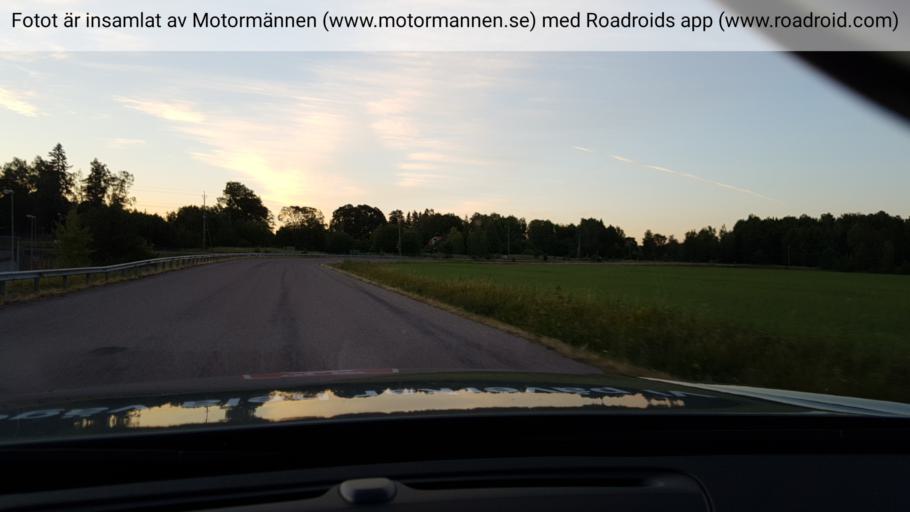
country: SE
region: Vaestmanland
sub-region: Hallstahammars Kommun
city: Kolback
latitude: 59.5341
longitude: 16.1431
